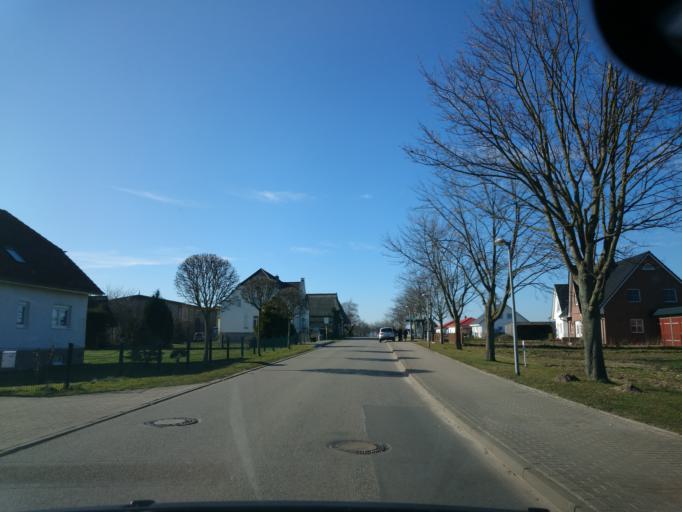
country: DE
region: Mecklenburg-Vorpommern
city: Borgerende-Rethwisch
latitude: 54.1428
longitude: 11.9196
